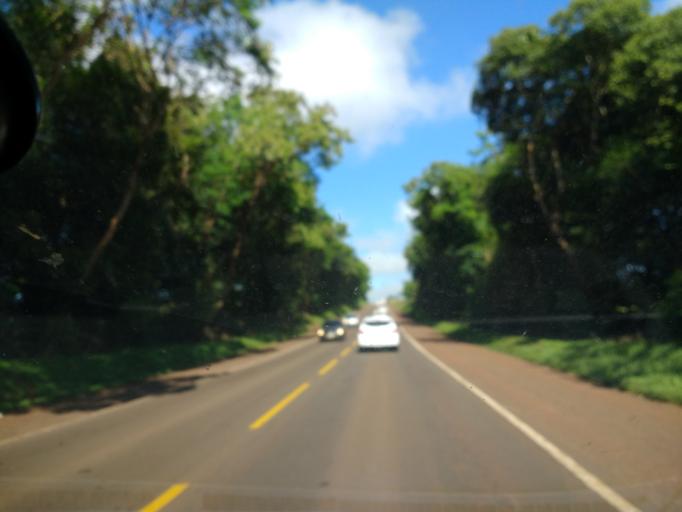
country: BR
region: Parana
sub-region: Paicandu
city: Paicandu
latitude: -23.5428
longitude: -52.2263
